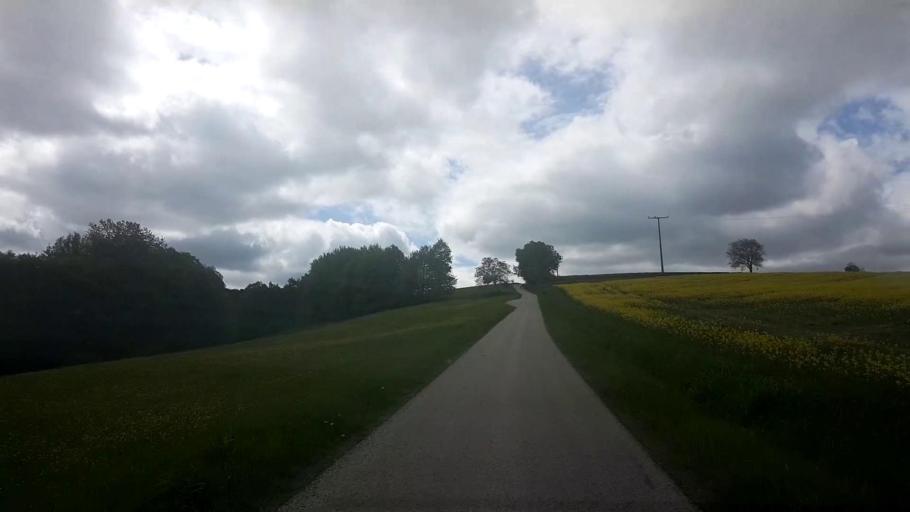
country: DE
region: Bavaria
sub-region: Upper Franconia
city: Bad Staffelstein
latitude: 50.1077
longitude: 11.0375
